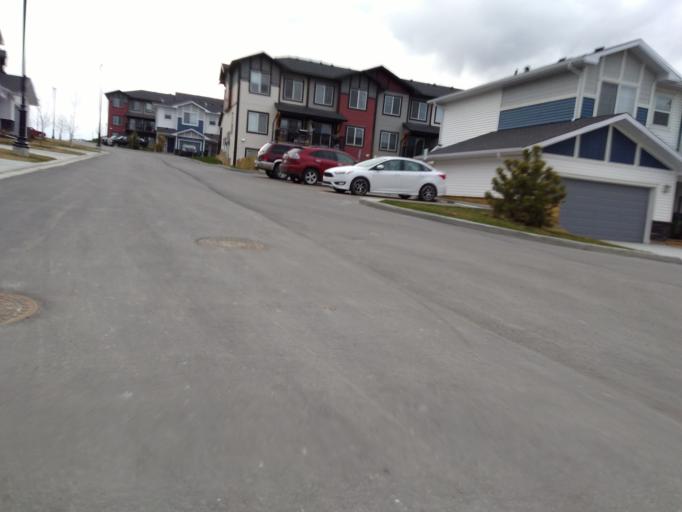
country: CA
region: Alberta
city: Cochrane
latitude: 51.1828
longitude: -114.5092
